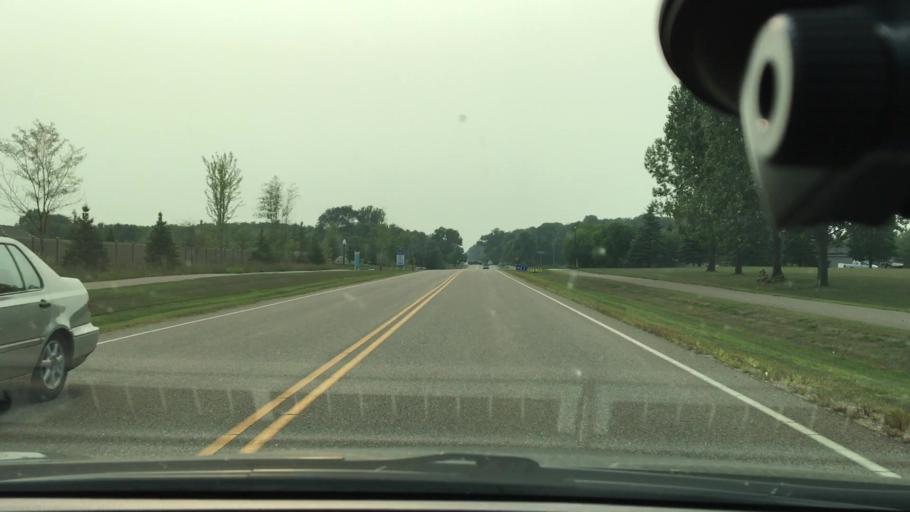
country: US
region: Minnesota
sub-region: Hennepin County
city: Champlin
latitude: 45.1990
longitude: -93.4377
